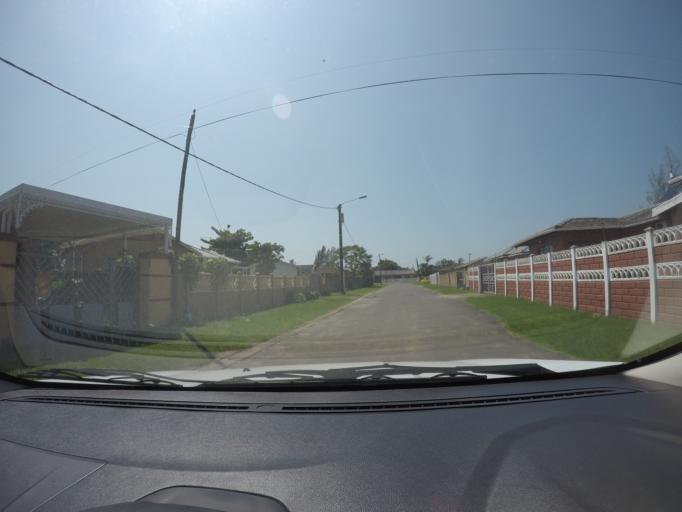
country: ZA
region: KwaZulu-Natal
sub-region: uThungulu District Municipality
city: eSikhawini
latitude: -28.8633
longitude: 31.9193
